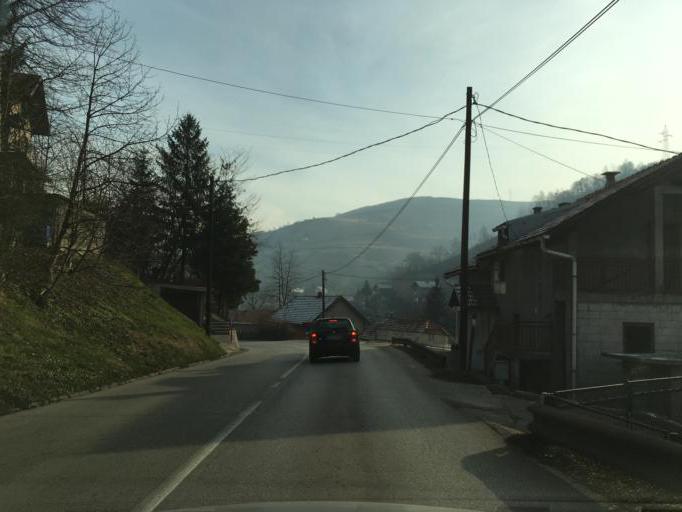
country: BA
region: Federation of Bosnia and Herzegovina
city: Zenica
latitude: 44.1931
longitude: 17.8843
